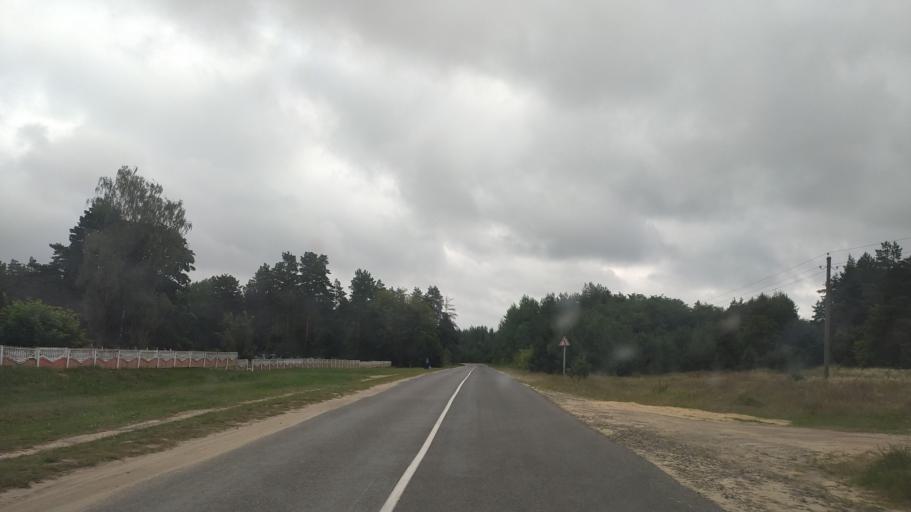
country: BY
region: Brest
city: Byaroza
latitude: 52.5984
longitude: 24.8751
